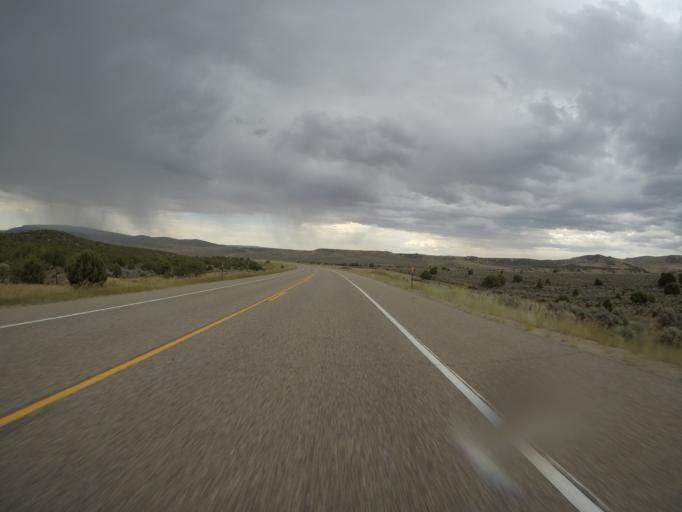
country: US
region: Colorado
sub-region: Rio Blanco County
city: Rangely
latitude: 40.3872
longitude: -108.3488
